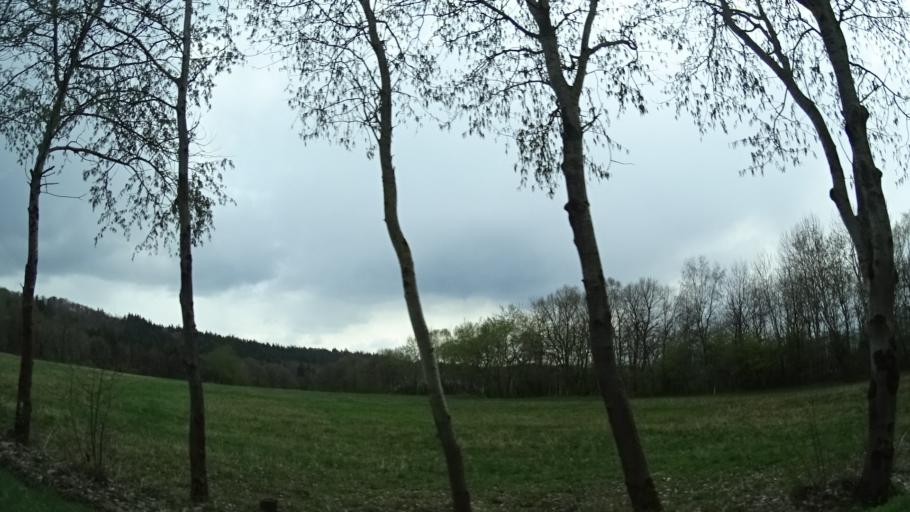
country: DE
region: Rheinland-Pfalz
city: Weitersborn
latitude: 49.8754
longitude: 7.5305
